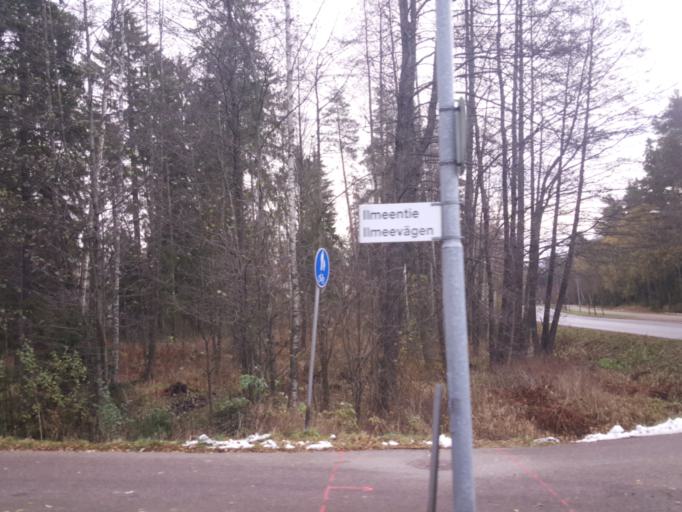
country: FI
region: Uusimaa
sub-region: Helsinki
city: Kilo
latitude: 60.2019
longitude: 24.7974
